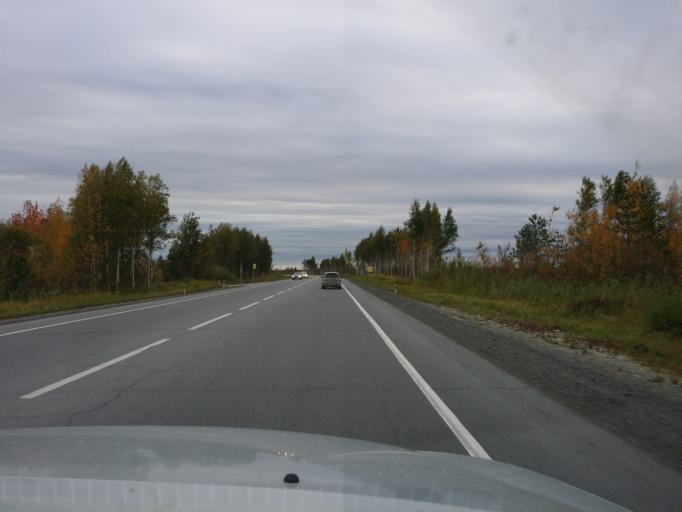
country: RU
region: Khanty-Mansiyskiy Avtonomnyy Okrug
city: Megion
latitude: 61.0677
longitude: 76.2529
